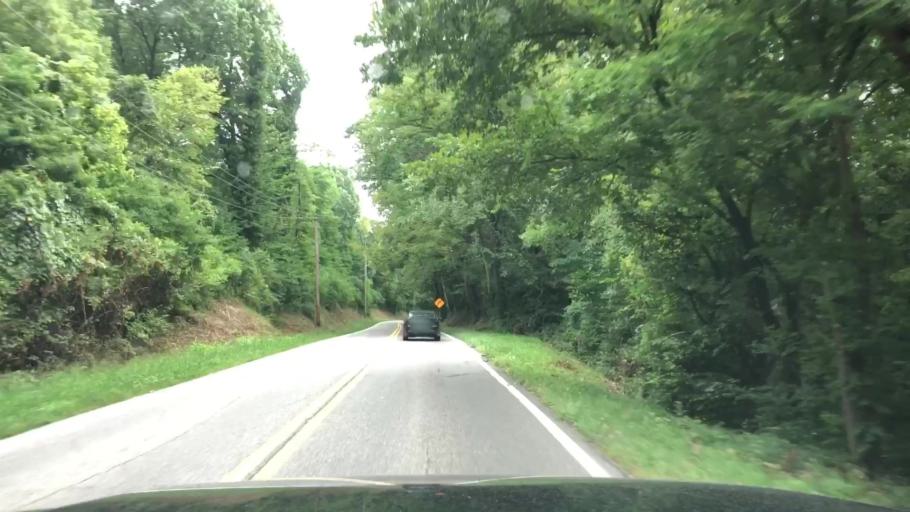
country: US
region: Missouri
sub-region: Saint Louis County
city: Hazelwood
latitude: 38.8109
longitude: -90.3889
